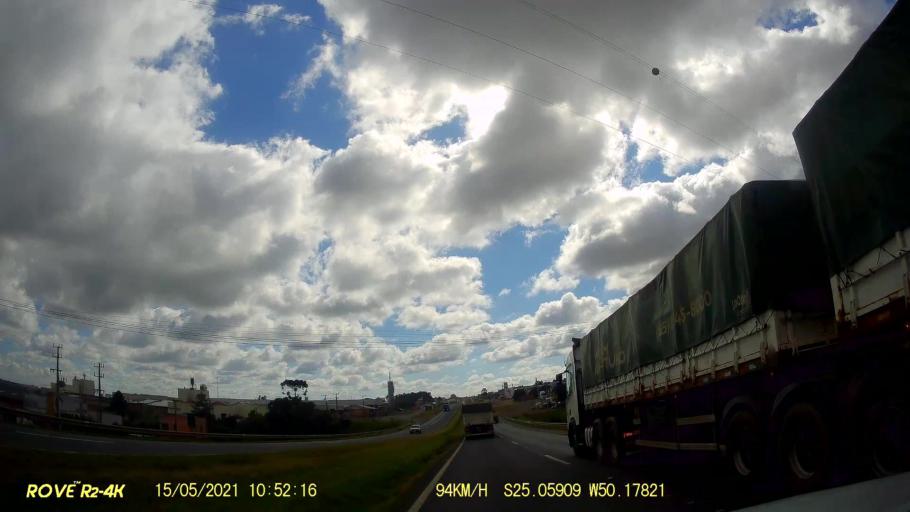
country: BR
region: Parana
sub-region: Ponta Grossa
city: Ponta Grossa
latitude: -25.0593
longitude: -50.1783
